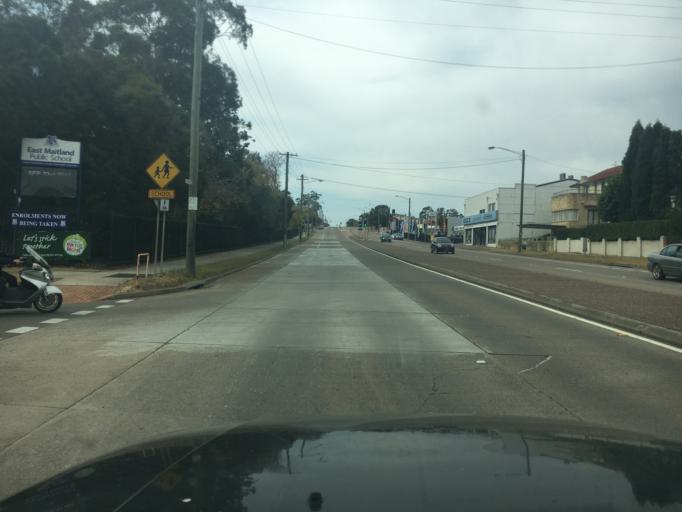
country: AU
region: New South Wales
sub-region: Maitland Municipality
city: East Maitland
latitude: -32.7490
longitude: 151.5836
